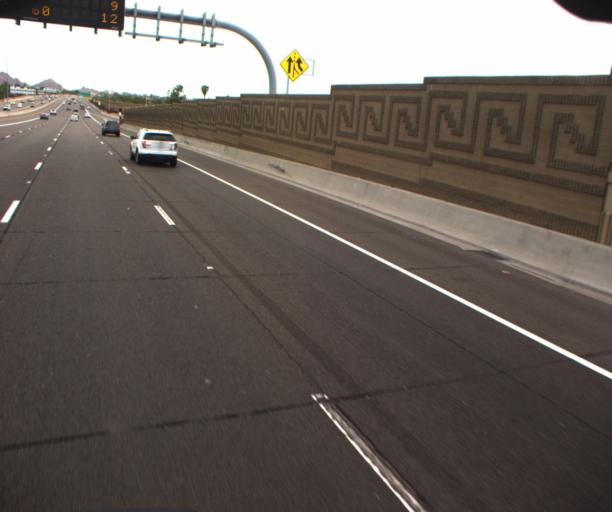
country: US
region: Arizona
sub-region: Maricopa County
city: Phoenix
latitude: 33.4619
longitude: -112.0289
